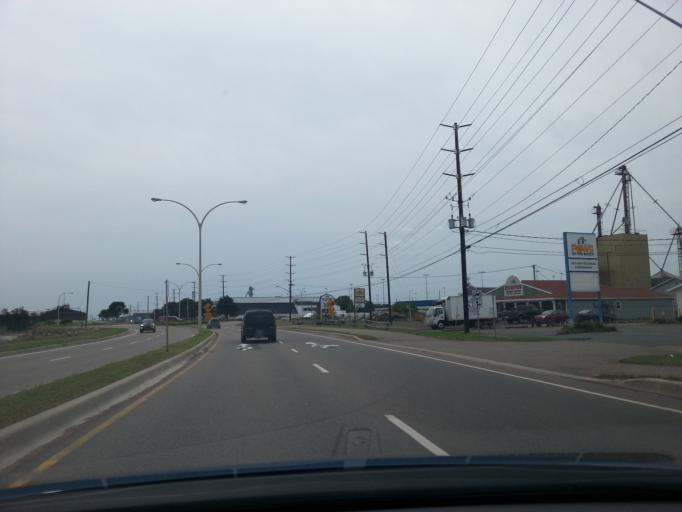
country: CA
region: Prince Edward Island
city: Charlottetown
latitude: 46.2493
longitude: -63.1111
